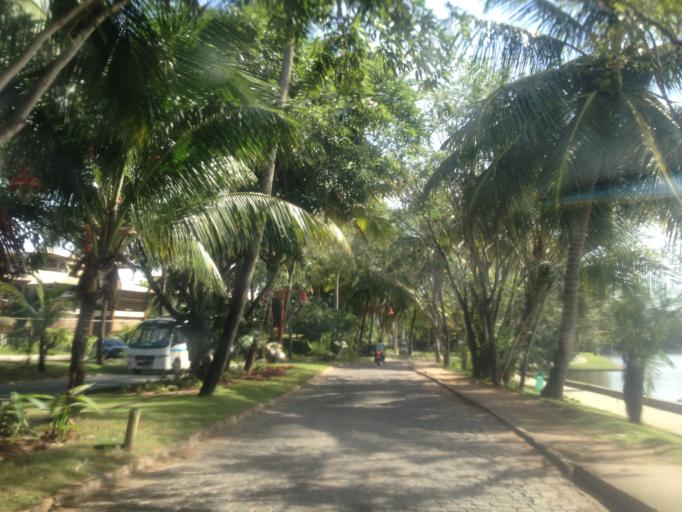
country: BR
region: Bahia
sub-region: Mata De Sao Joao
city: Mata de Sao Joao
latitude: -12.5781
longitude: -38.0119
